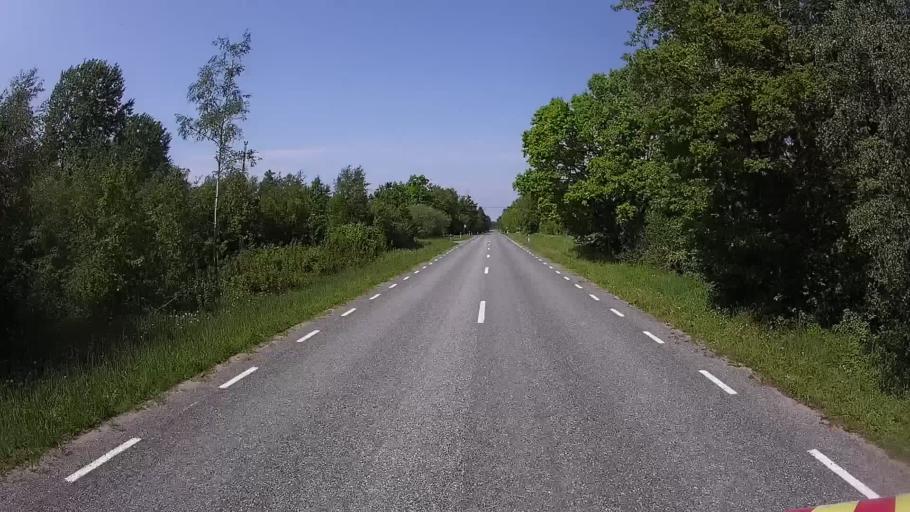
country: EE
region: Saare
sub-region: Kuressaare linn
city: Kuressaare
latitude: 58.3723
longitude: 22.0438
